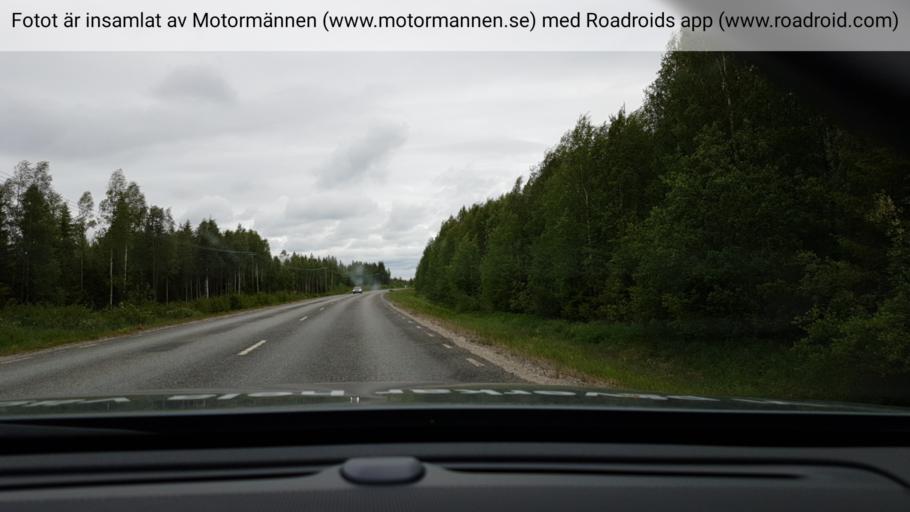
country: SE
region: Vaesterbotten
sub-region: Lycksele Kommun
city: Lycksele
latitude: 64.5556
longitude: 18.5155
